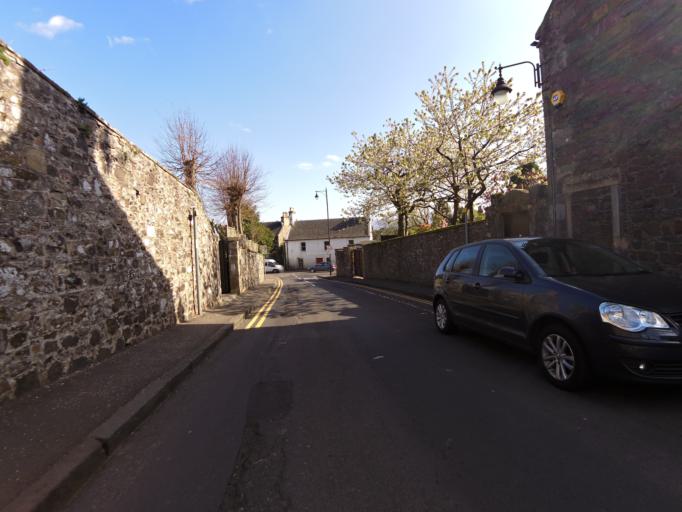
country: GB
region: Scotland
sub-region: Fife
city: Auchtermuchty
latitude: 56.2912
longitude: -3.2311
